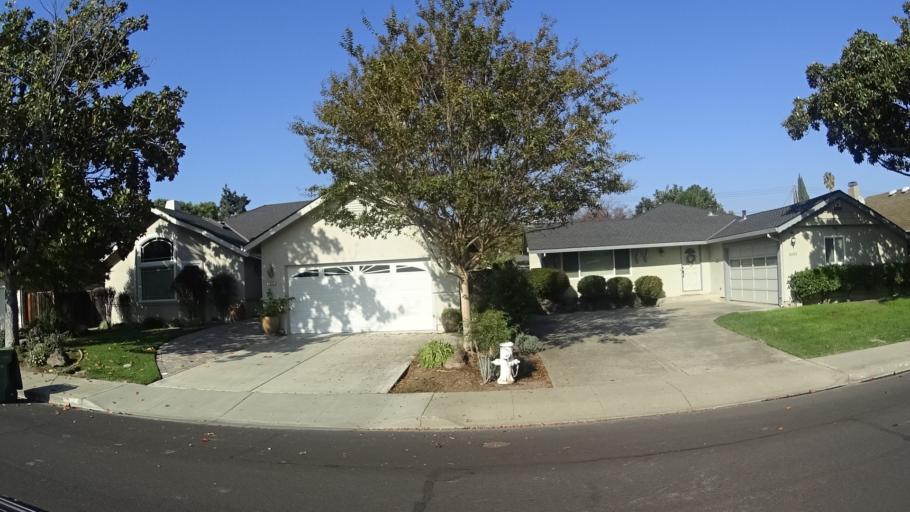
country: US
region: California
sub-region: Santa Clara County
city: Santa Clara
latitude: 37.3640
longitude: -121.9903
